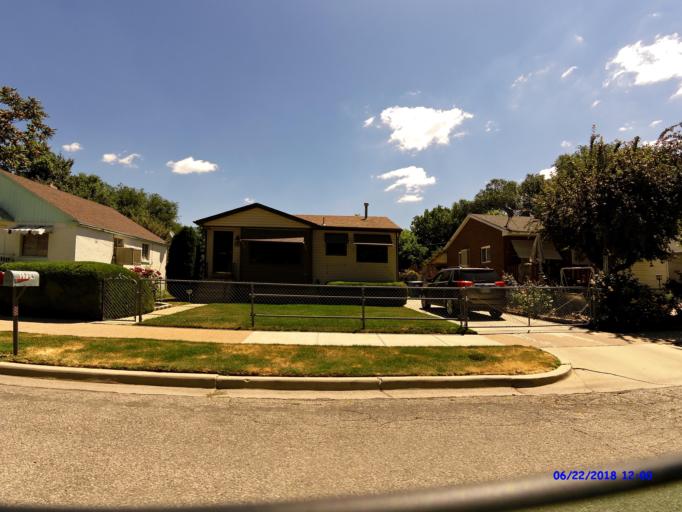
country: US
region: Utah
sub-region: Weber County
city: Ogden
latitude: 41.2361
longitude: -111.9743
